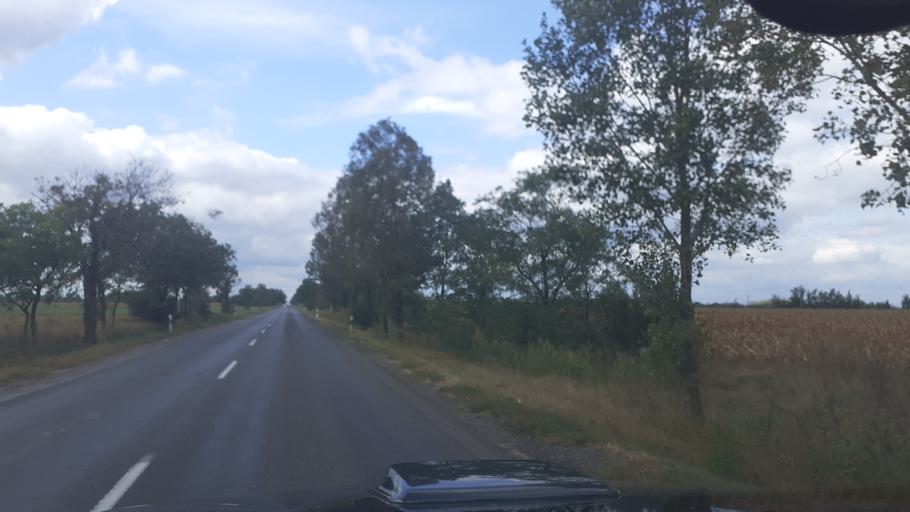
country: HU
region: Bacs-Kiskun
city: Solt
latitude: 46.7984
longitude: 19.1080
